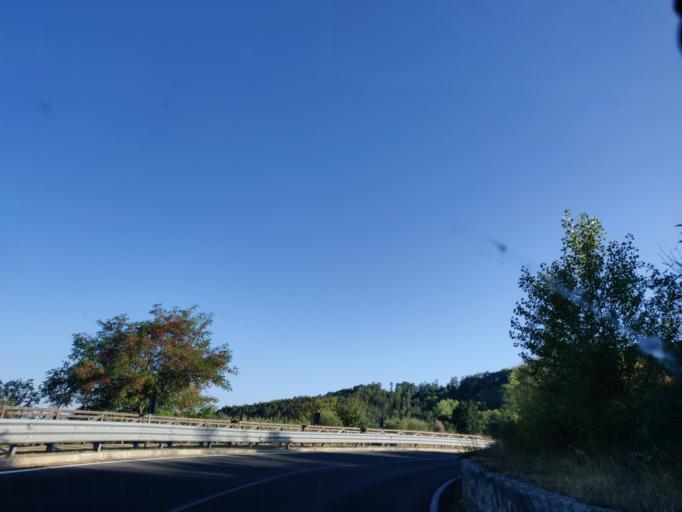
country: IT
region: Tuscany
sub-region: Provincia di Siena
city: Abbadia San Salvatore
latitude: 42.8654
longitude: 11.6796
